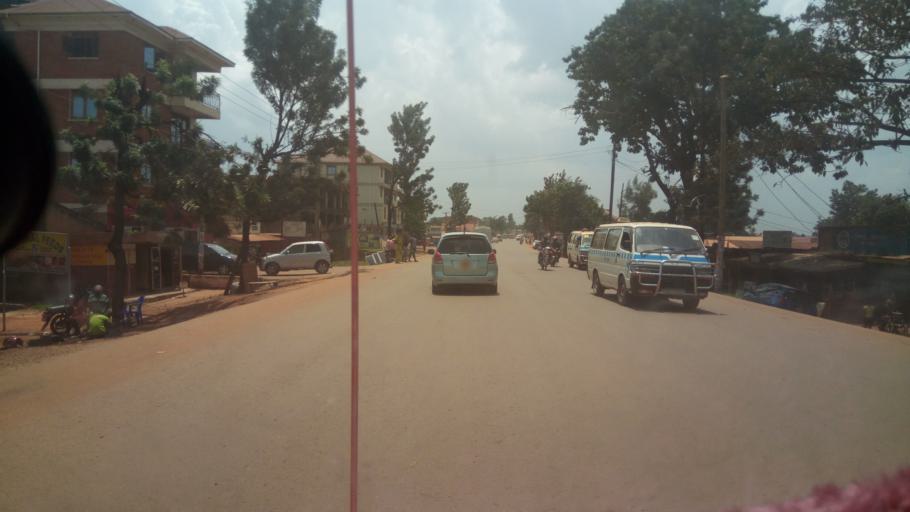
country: UG
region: Central Region
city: Kampala Central Division
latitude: 0.3593
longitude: 32.5319
